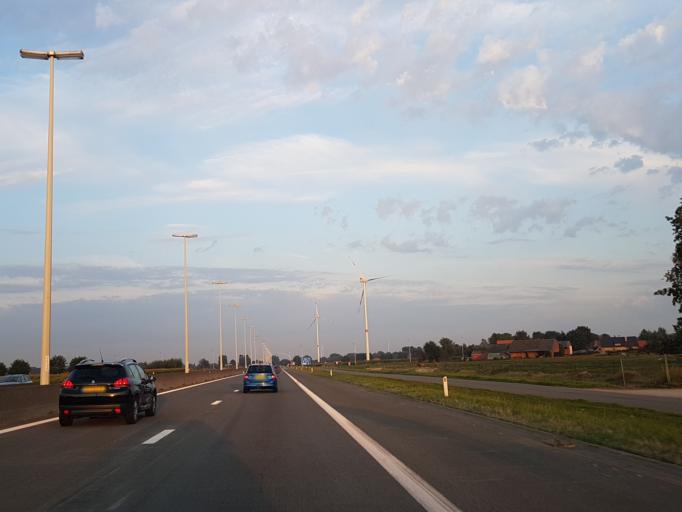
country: BE
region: Flanders
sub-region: Provincie Oost-Vlaanderen
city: Assenede
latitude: 51.2046
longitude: 3.7020
